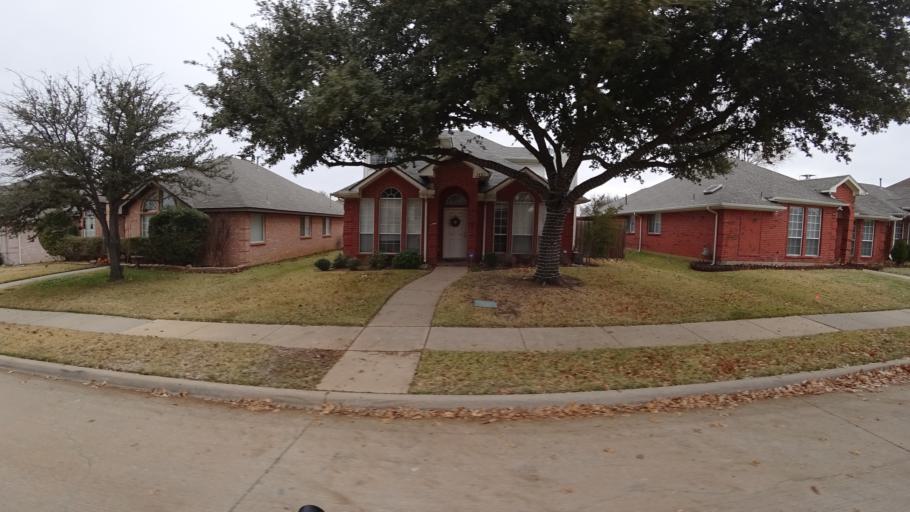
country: US
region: Texas
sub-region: Denton County
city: Lewisville
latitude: 33.0296
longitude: -97.0354
